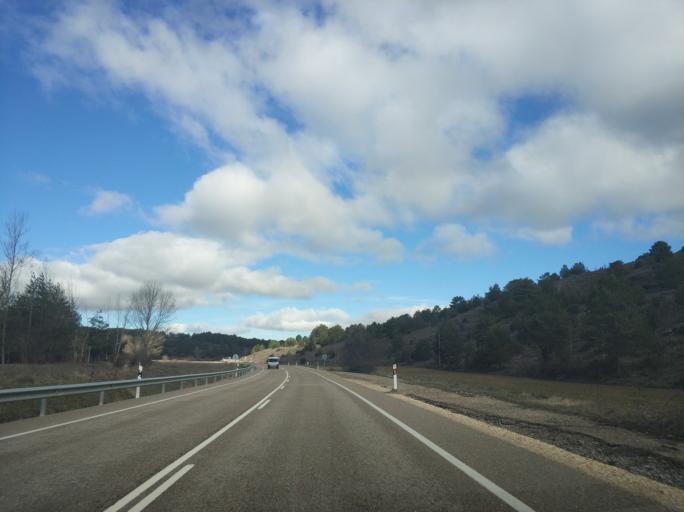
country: ES
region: Castille and Leon
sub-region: Provincia de Burgos
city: Rabanera del Pinar
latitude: 41.8704
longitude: -3.2155
